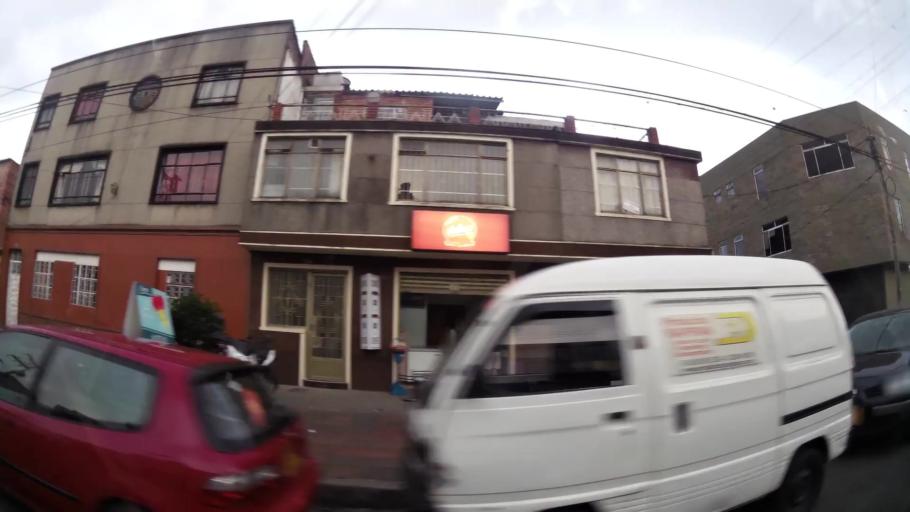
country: CO
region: Bogota D.C.
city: Barrio San Luis
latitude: 4.6701
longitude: -74.0795
